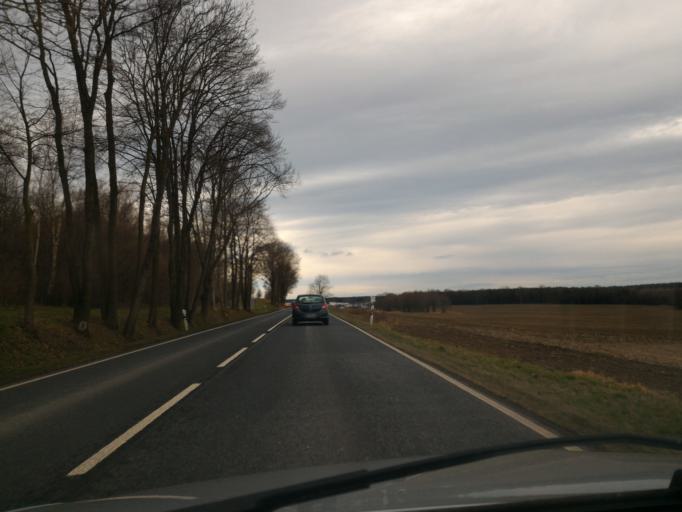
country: DE
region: Saxony
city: Radeberg
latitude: 51.0621
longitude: 13.9114
